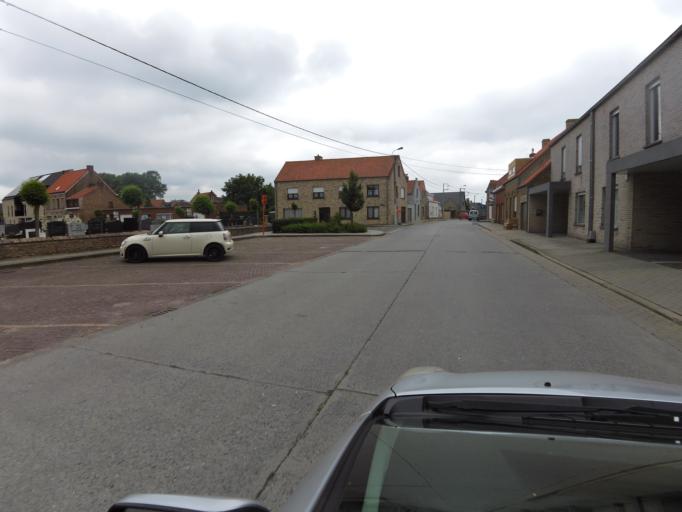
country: BE
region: Flanders
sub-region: Provincie West-Vlaanderen
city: Diksmuide
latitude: 51.0015
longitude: 2.8712
